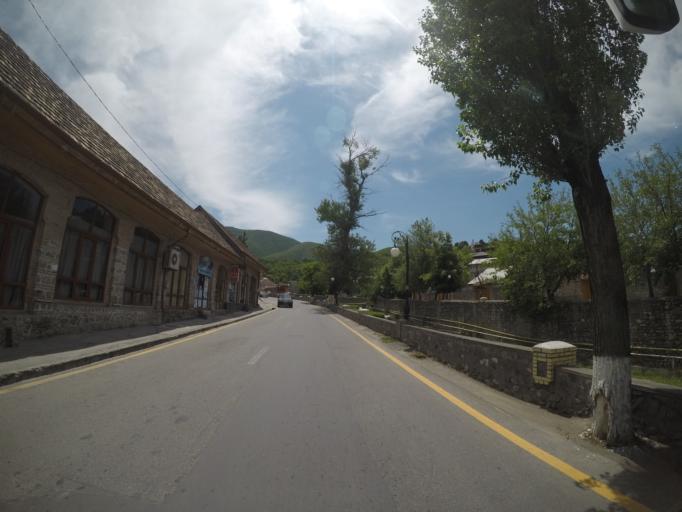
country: AZ
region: Shaki City
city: Sheki
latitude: 41.2010
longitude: 47.1849
